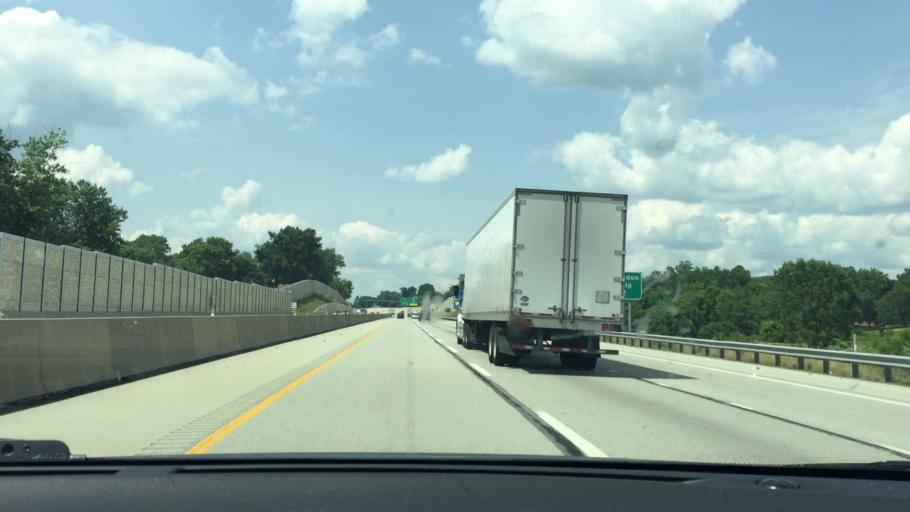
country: US
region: Pennsylvania
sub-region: Westmoreland County
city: Manor
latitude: 40.2993
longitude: -79.6716
